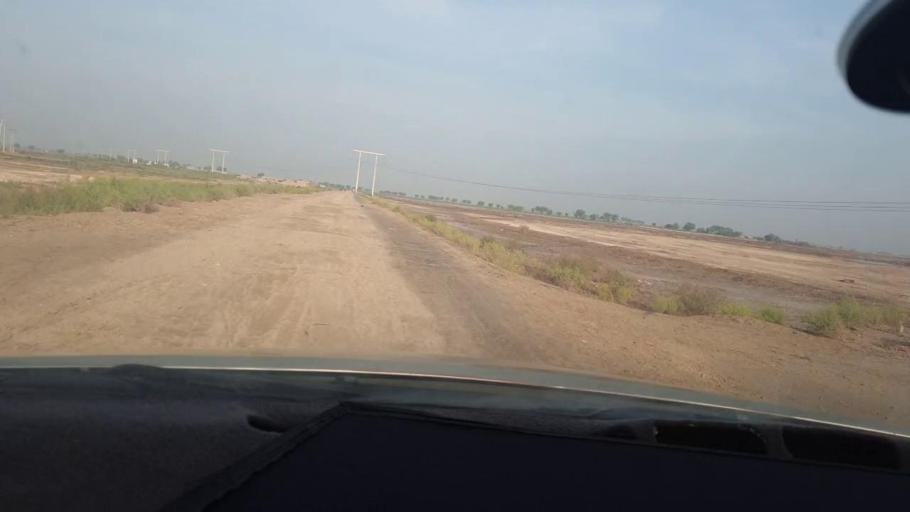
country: PK
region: Sindh
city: Jacobabad
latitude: 28.3346
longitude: 68.4127
